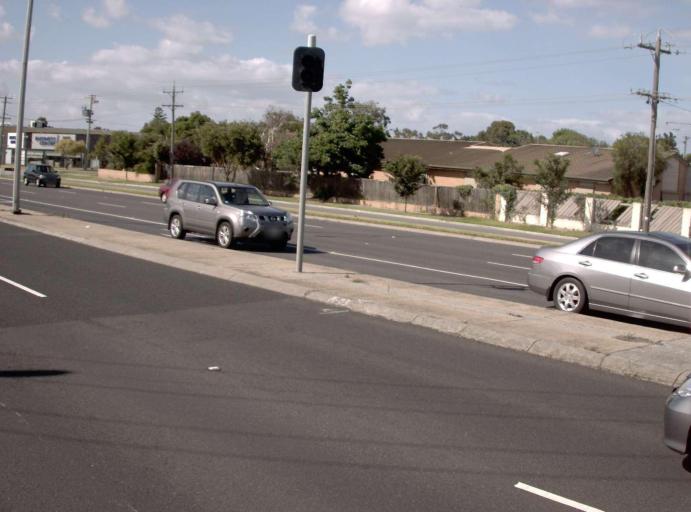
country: AU
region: Victoria
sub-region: Kingston
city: Mentone
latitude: -37.9737
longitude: 145.0644
